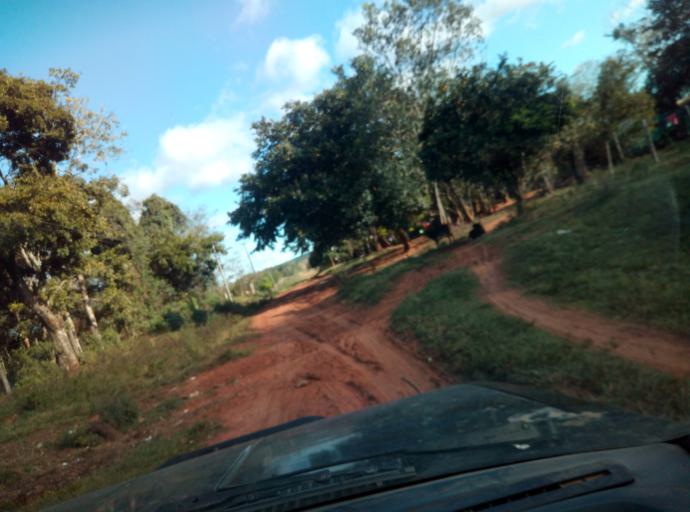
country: PY
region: Caaguazu
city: Doctor Cecilio Baez
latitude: -25.1644
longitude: -56.2724
